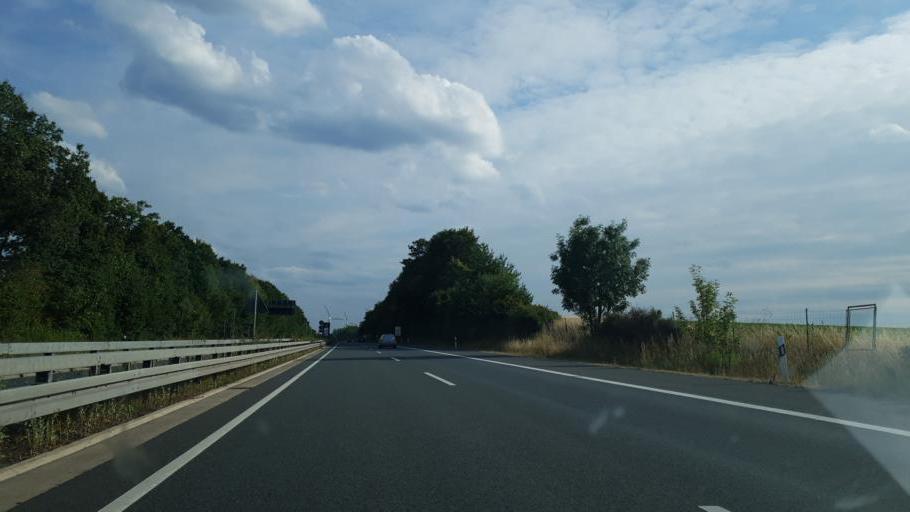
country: DE
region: Lower Saxony
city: Holle
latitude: 52.0977
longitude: 10.1821
